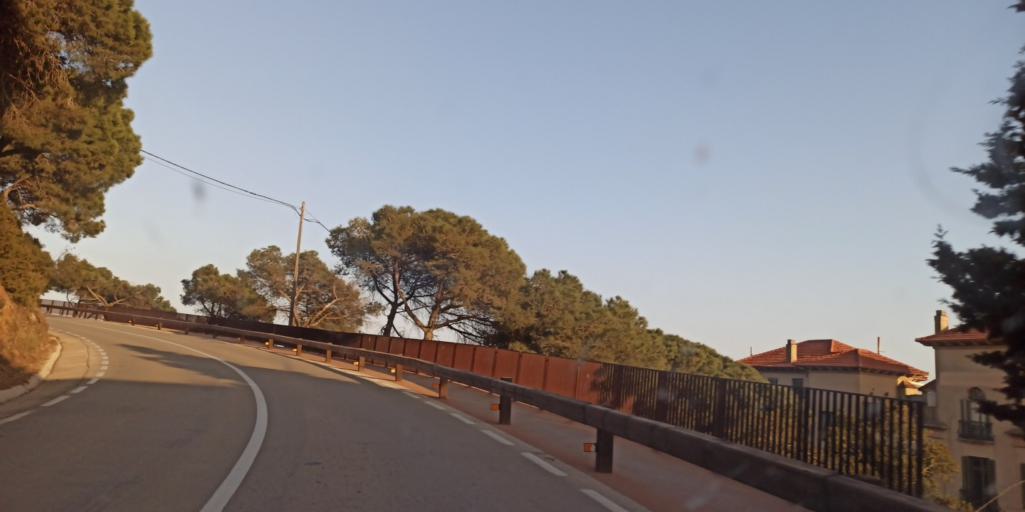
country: ES
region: Catalonia
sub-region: Provincia de Barcelona
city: Sarria-Sant Gervasi
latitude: 41.4161
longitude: 2.1139
